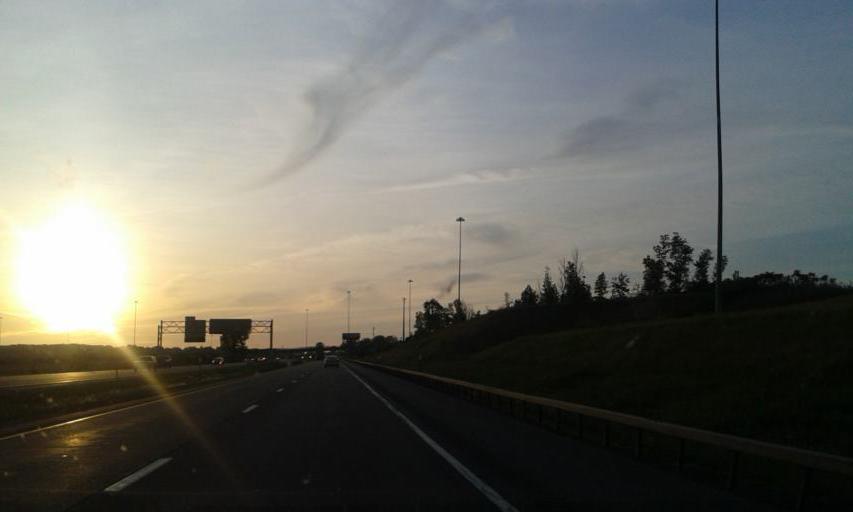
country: US
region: New York
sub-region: Onondaga County
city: Solvay
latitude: 43.0768
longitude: -76.2146
